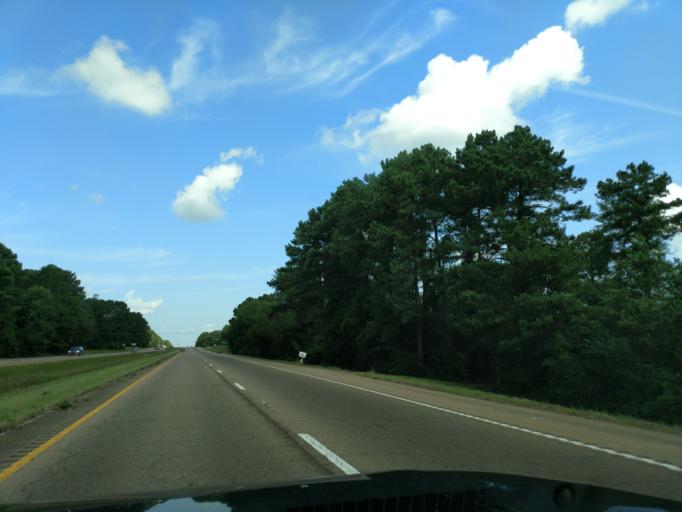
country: US
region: Mississippi
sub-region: Simpson County
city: Magee
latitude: 31.9023
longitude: -89.7775
